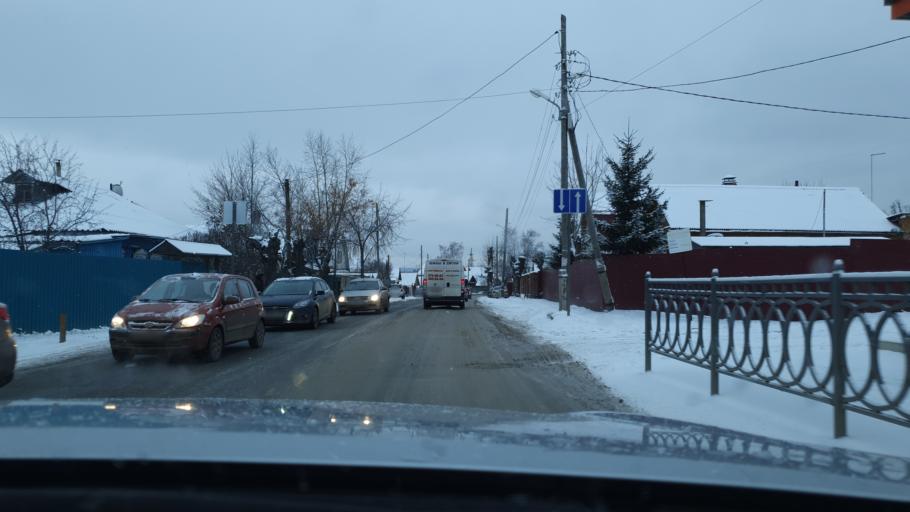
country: RU
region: Sverdlovsk
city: Istok
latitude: 56.7833
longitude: 60.7432
